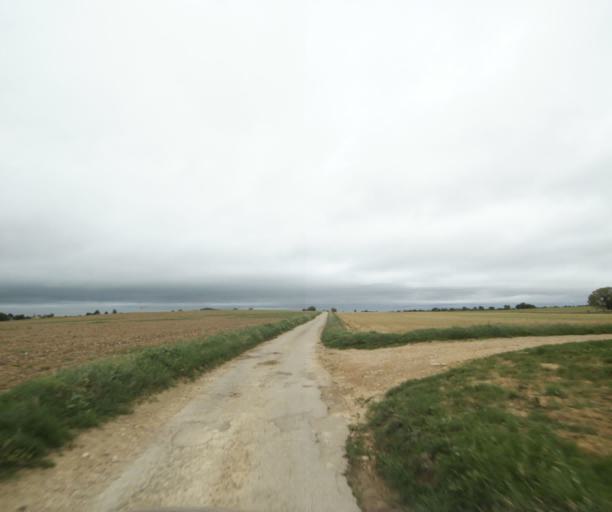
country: FR
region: Rhone-Alpes
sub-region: Departement de l'Ain
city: Miribel
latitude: 45.8383
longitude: 4.9341
